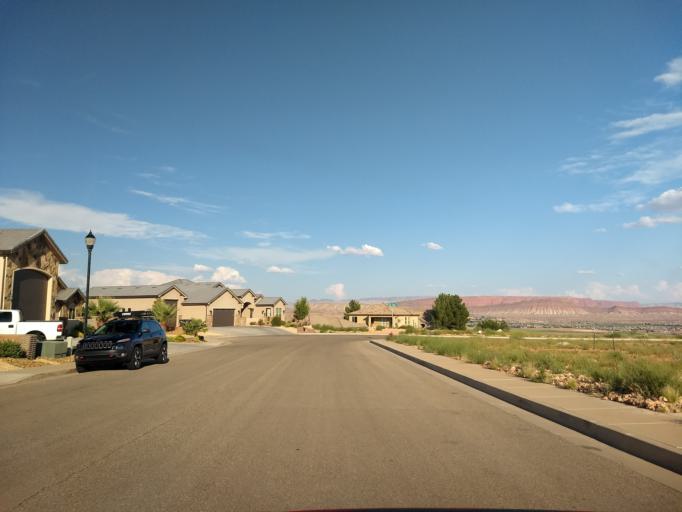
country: US
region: Utah
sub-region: Washington County
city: Saint George
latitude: 37.1024
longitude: -113.5474
